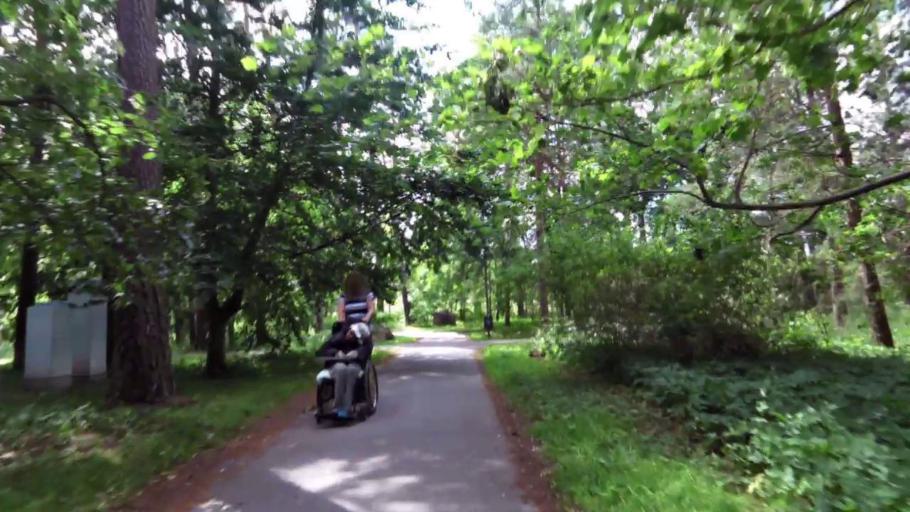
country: SE
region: OEstergoetland
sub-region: Linkopings Kommun
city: Linkoping
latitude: 58.4114
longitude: 15.5977
